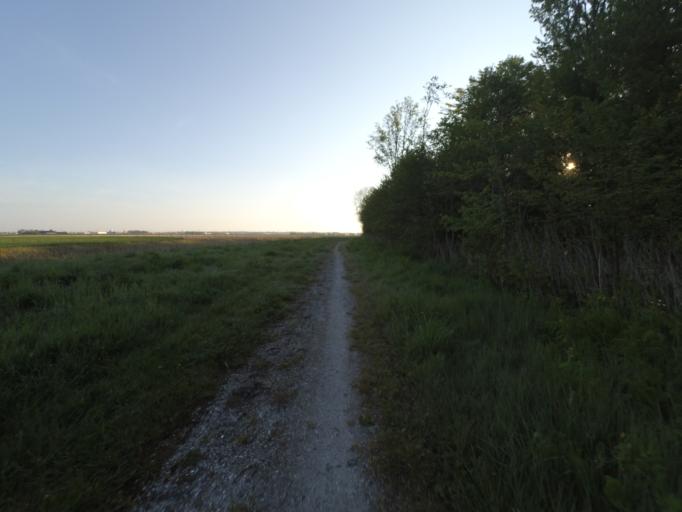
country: NL
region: Flevoland
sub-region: Gemeente Lelystad
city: Lelystad
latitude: 52.4490
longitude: 5.4917
